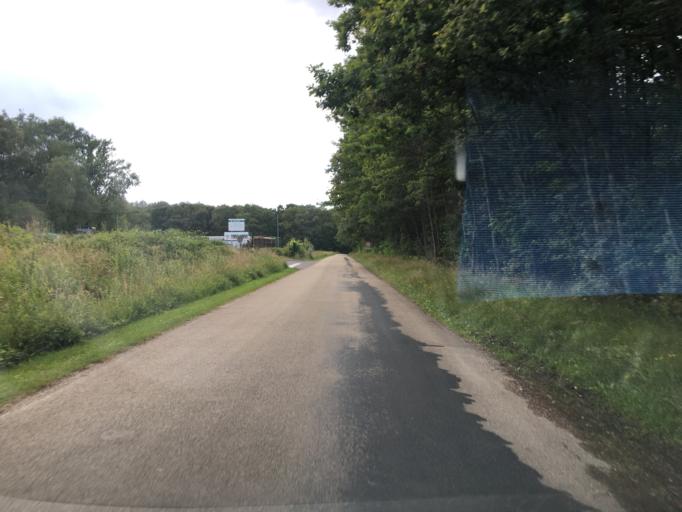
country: FR
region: Bourgogne
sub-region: Departement de l'Yonne
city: Charbuy
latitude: 47.8474
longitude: 3.4944
